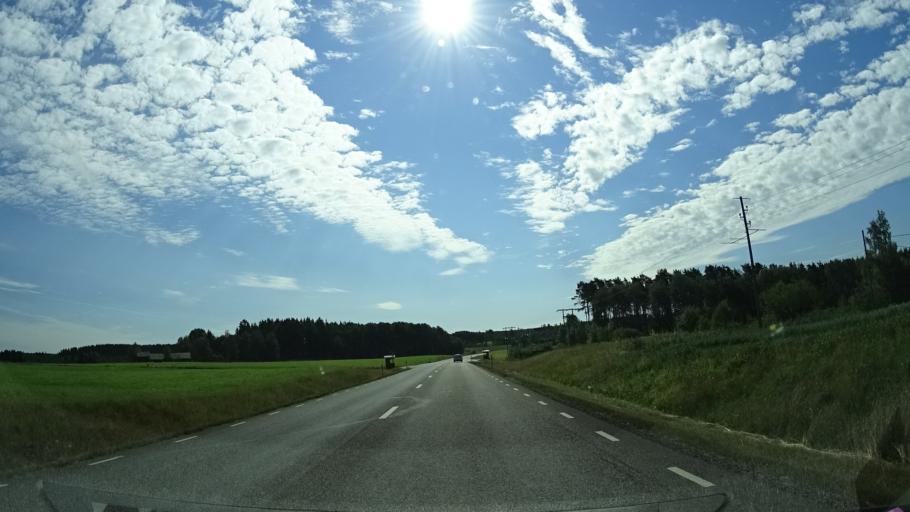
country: SE
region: Vaermland
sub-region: Arjangs Kommun
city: Toecksfors
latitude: 59.4692
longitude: 11.9949
